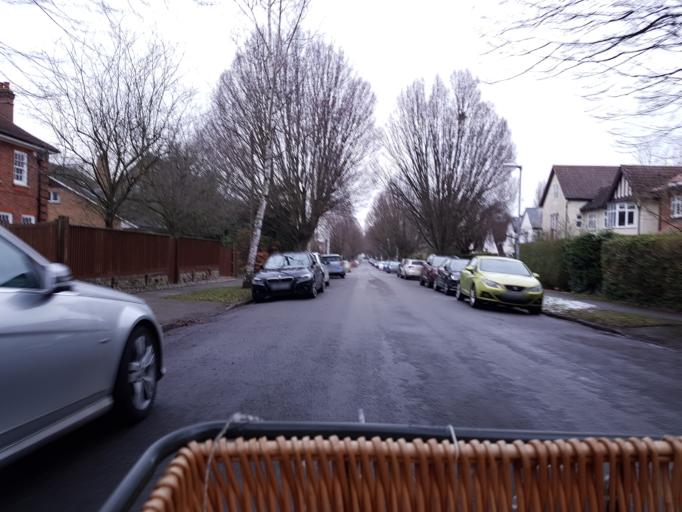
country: GB
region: England
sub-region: Cambridgeshire
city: Cambridge
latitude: 52.1838
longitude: 0.1421
